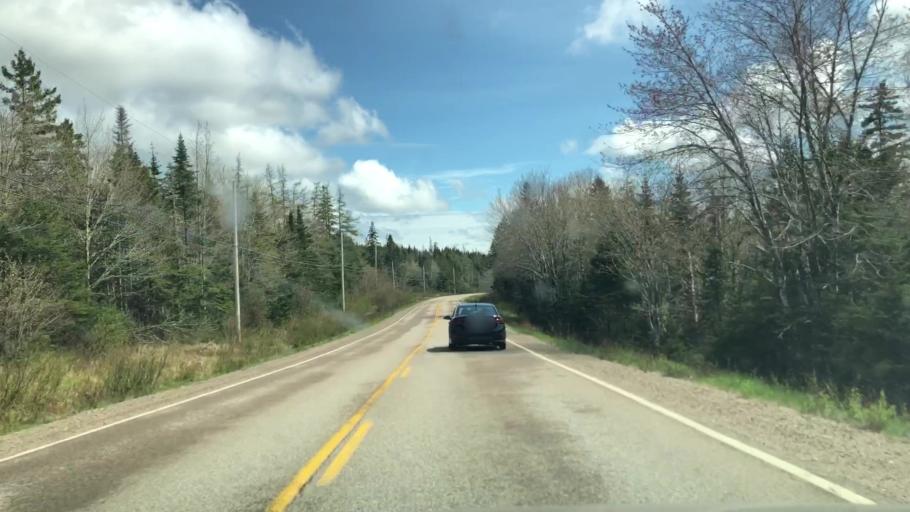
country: CA
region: Nova Scotia
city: Antigonish
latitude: 45.2118
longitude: -62.0048
